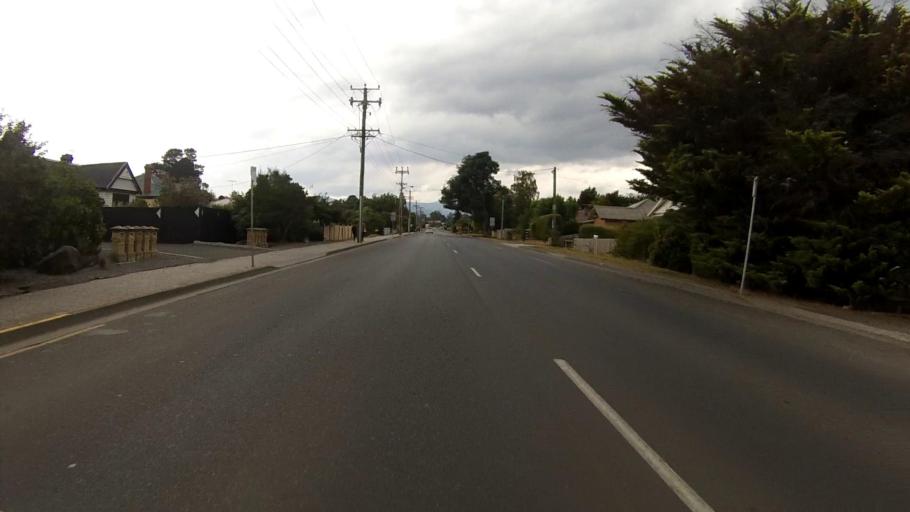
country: AU
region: Tasmania
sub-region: Huon Valley
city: Huonville
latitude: -43.0263
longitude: 147.0509
